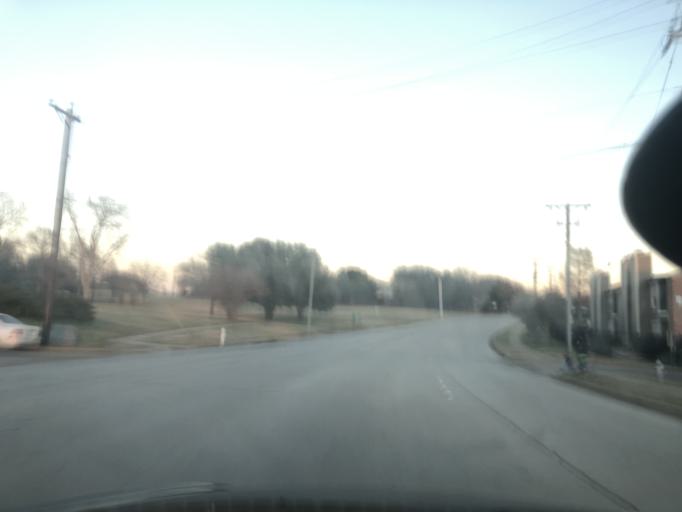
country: US
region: Texas
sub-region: Tarrant County
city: White Settlement
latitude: 32.7351
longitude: -97.4758
